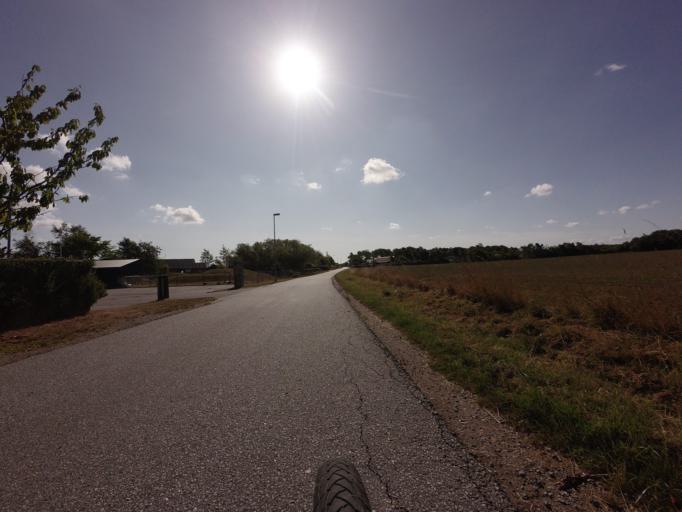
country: DK
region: North Denmark
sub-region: Hjorring Kommune
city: Vra
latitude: 57.3966
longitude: 9.9828
